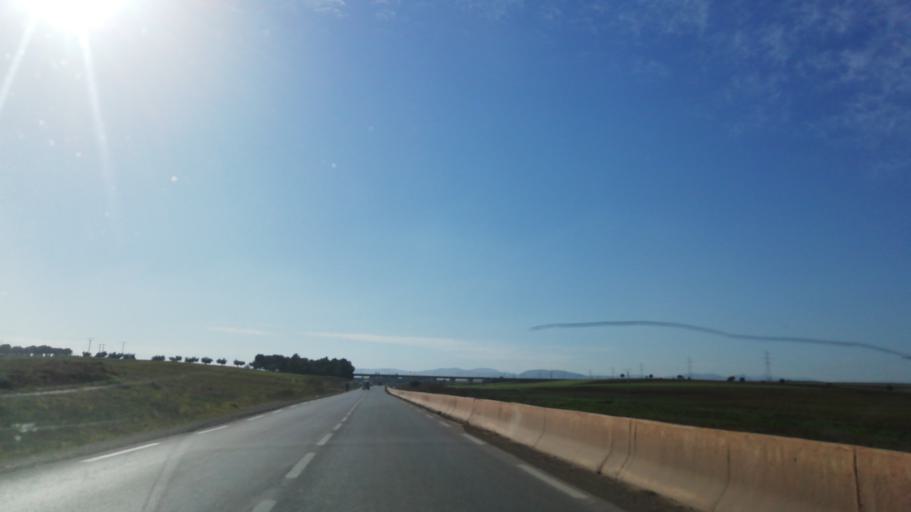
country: DZ
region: Tlemcen
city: Ouled Mimoun
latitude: 35.0159
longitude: -0.9049
